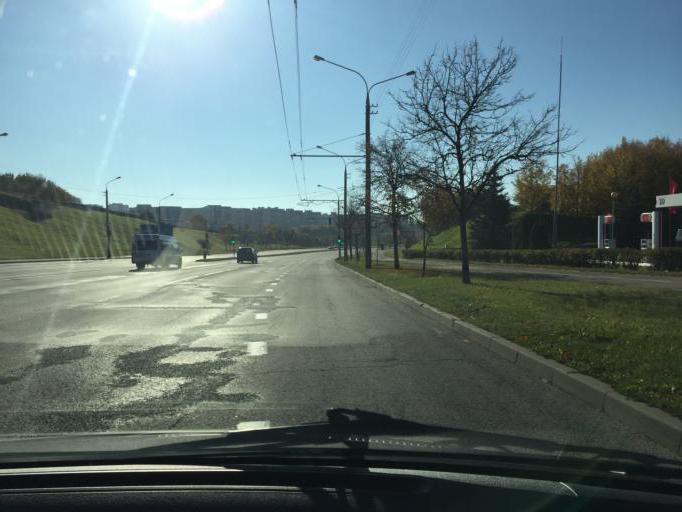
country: BY
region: Minsk
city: Syenitsa
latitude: 53.8593
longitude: 27.5378
